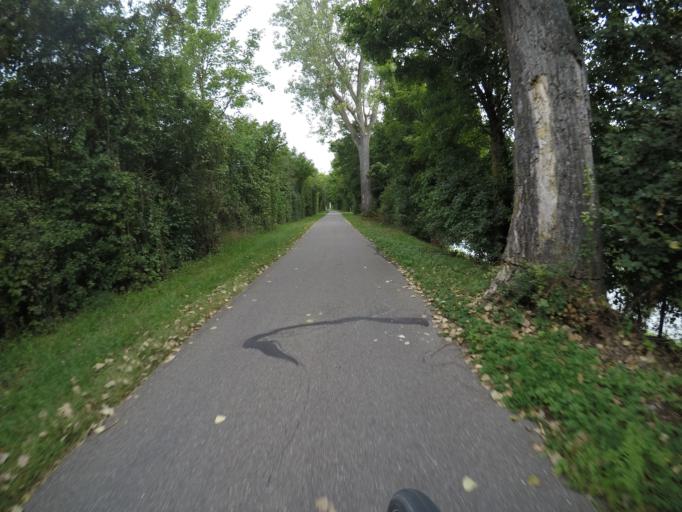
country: DE
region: Baden-Wuerttemberg
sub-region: Regierungsbezirk Stuttgart
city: Stuttgart Muehlhausen
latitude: 48.8575
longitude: 9.2518
